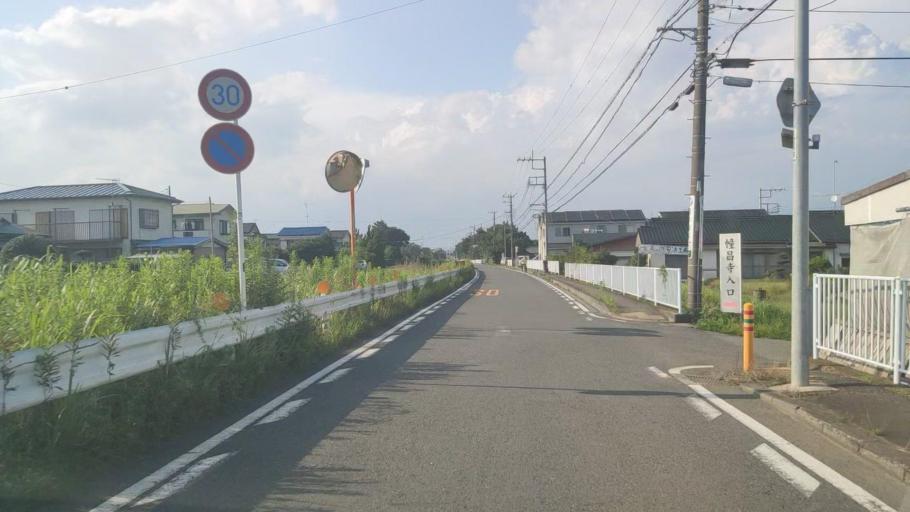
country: JP
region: Kanagawa
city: Isehara
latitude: 35.3849
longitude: 139.3388
